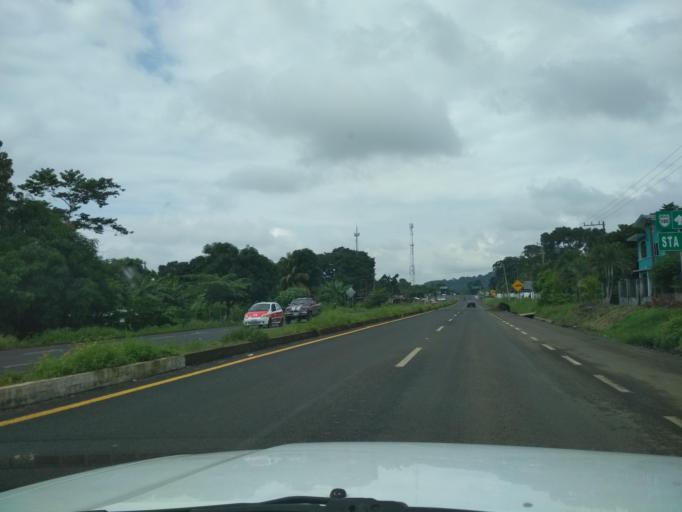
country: MX
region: Veracruz
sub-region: San Andres Tuxtla
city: Matacapan
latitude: 18.4349
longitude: -95.1669
